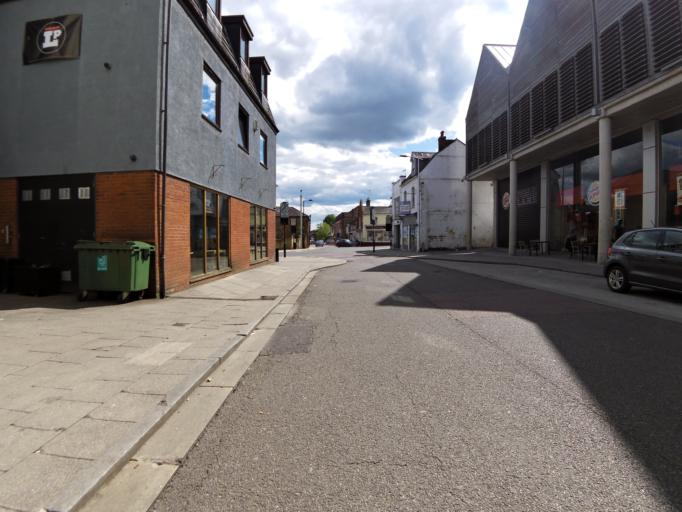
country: GB
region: England
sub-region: Suffolk
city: Bury St Edmunds
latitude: 52.2452
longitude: 0.7111
